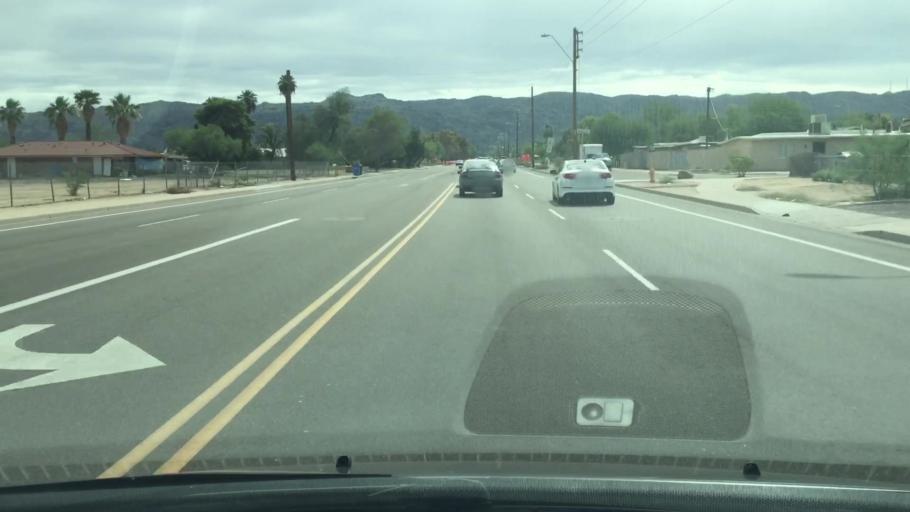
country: US
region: Arizona
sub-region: Maricopa County
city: Guadalupe
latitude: 33.3925
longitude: -112.0301
